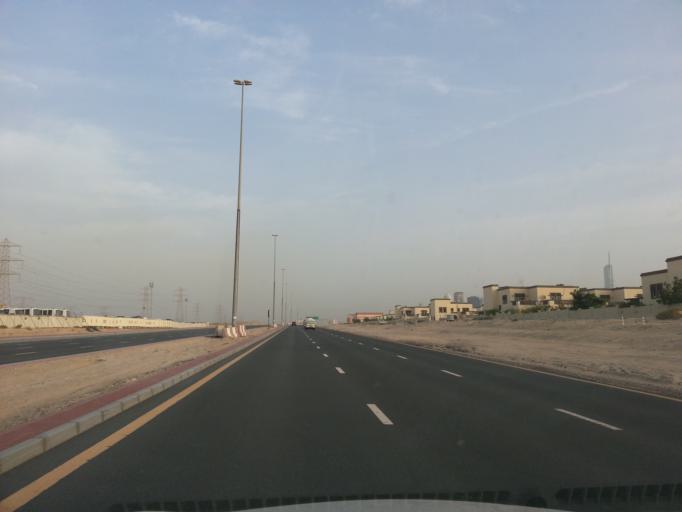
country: AE
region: Dubai
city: Dubai
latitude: 25.0459
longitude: 55.1497
